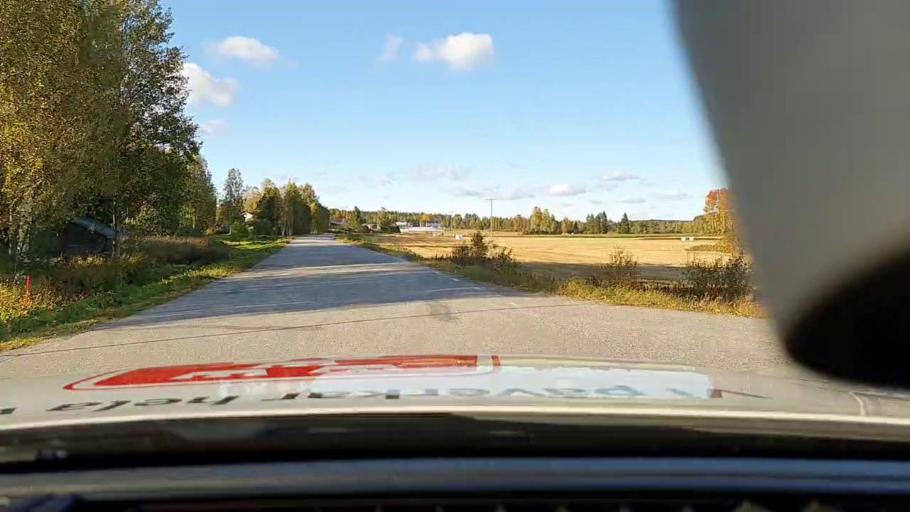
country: SE
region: Norrbotten
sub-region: Pitea Kommun
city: Norrfjarden
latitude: 65.5203
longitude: 21.4946
